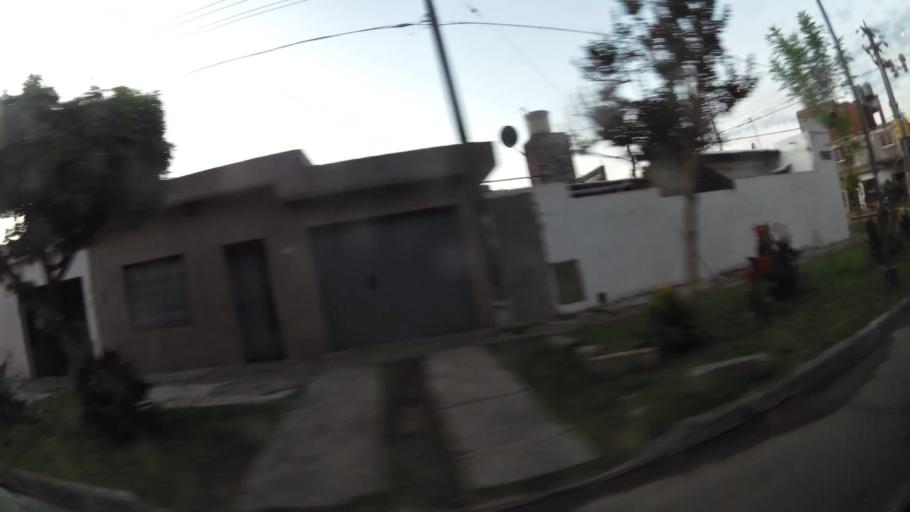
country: AR
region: Buenos Aires
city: San Nicolas de los Arroyos
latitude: -33.3458
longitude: -60.1926
